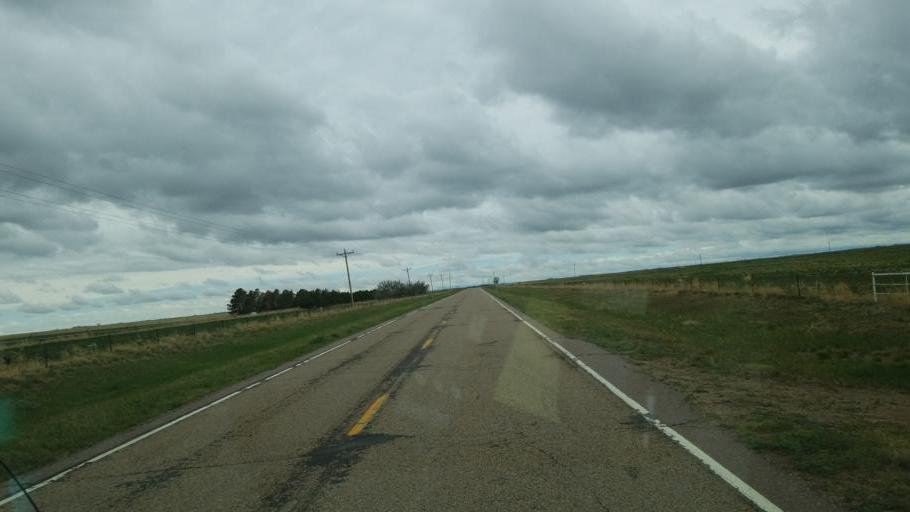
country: US
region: Colorado
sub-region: El Paso County
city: Ellicott
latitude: 38.8398
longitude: -103.9745
